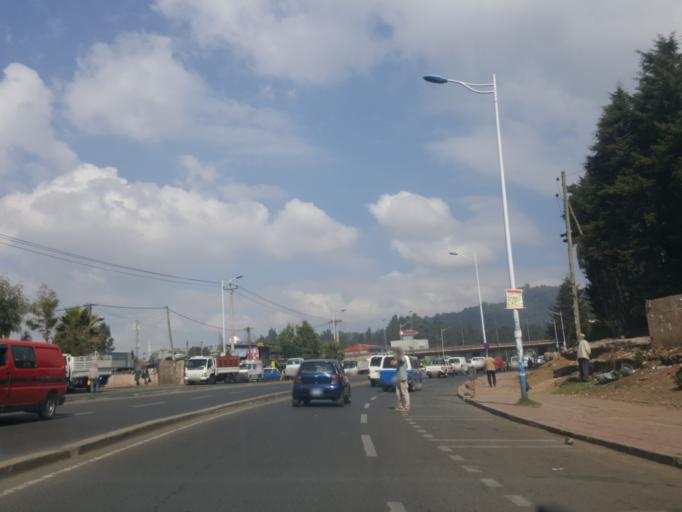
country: ET
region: Adis Abeba
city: Addis Ababa
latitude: 9.0548
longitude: 38.7141
